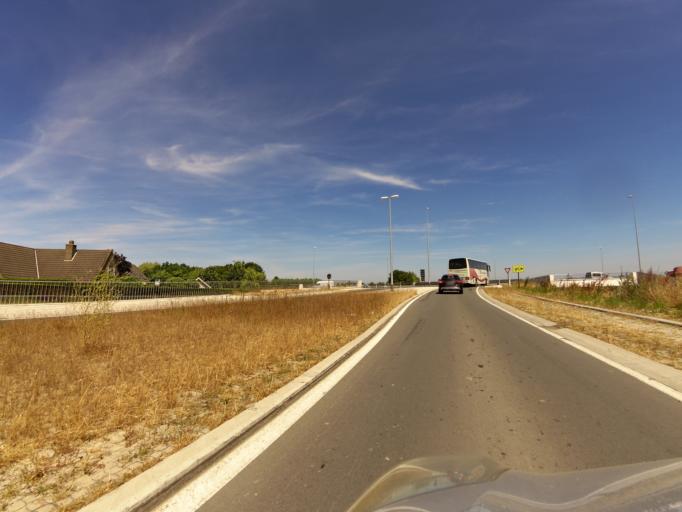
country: BE
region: Flanders
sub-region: Provincie West-Vlaanderen
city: Knokke-Heist
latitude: 51.3143
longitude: 3.3095
